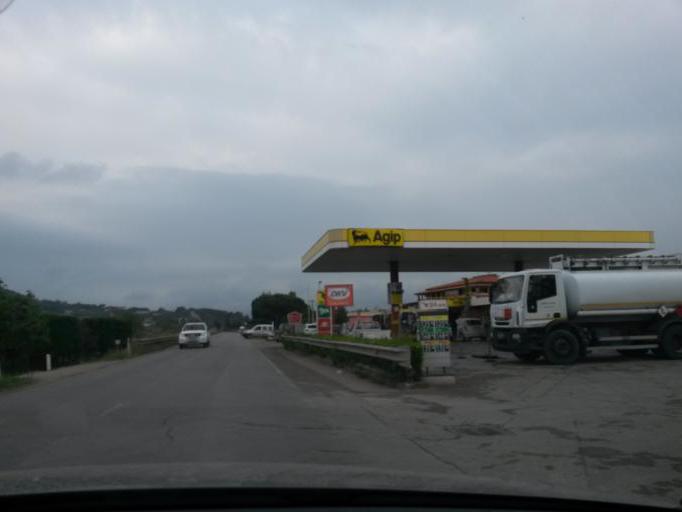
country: IT
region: Tuscany
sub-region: Provincia di Livorno
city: Capoliveri
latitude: 42.7591
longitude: 10.3782
